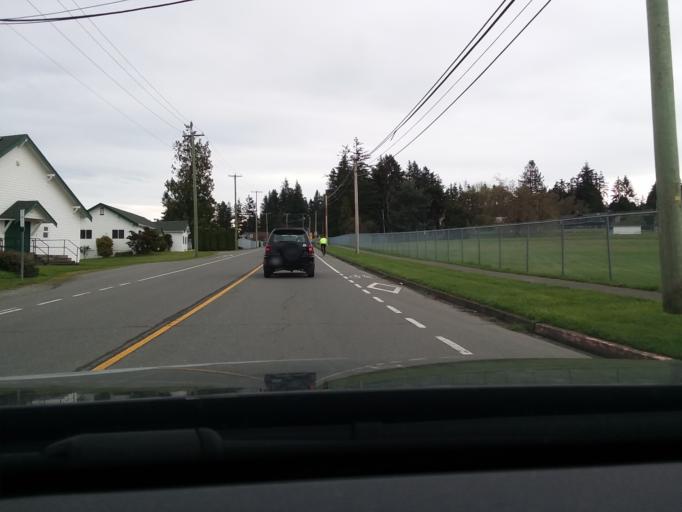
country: CA
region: British Columbia
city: North Saanich
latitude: 48.6209
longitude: -123.4176
